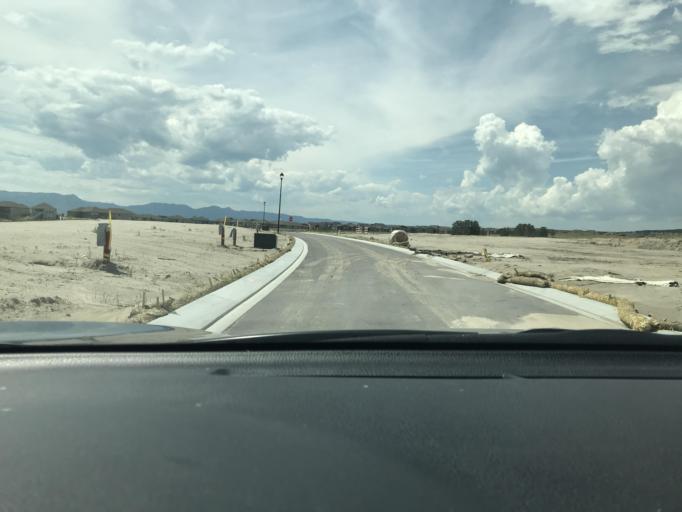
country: US
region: Colorado
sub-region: El Paso County
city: Black Forest
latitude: 38.9619
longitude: -104.7075
